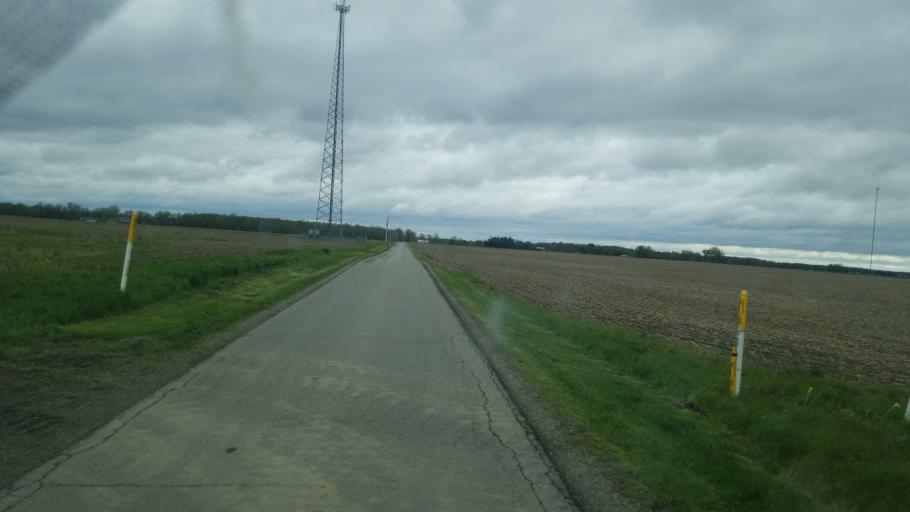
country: US
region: Ohio
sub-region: Crawford County
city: Bucyrus
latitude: 40.7391
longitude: -83.0735
